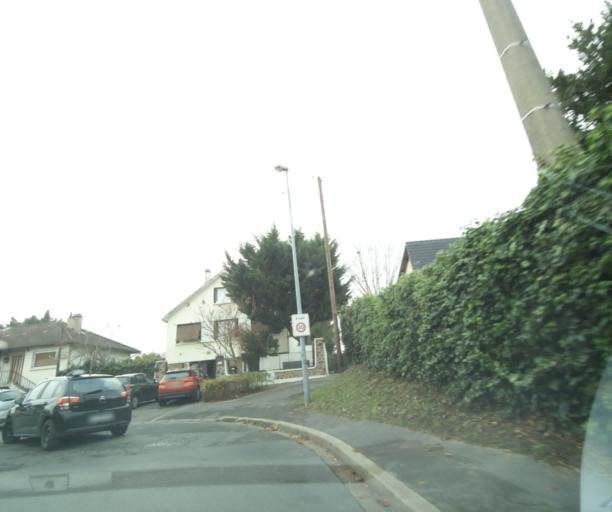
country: FR
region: Ile-de-France
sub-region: Departement de Seine-Saint-Denis
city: Villemomble
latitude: 48.8911
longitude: 2.4972
